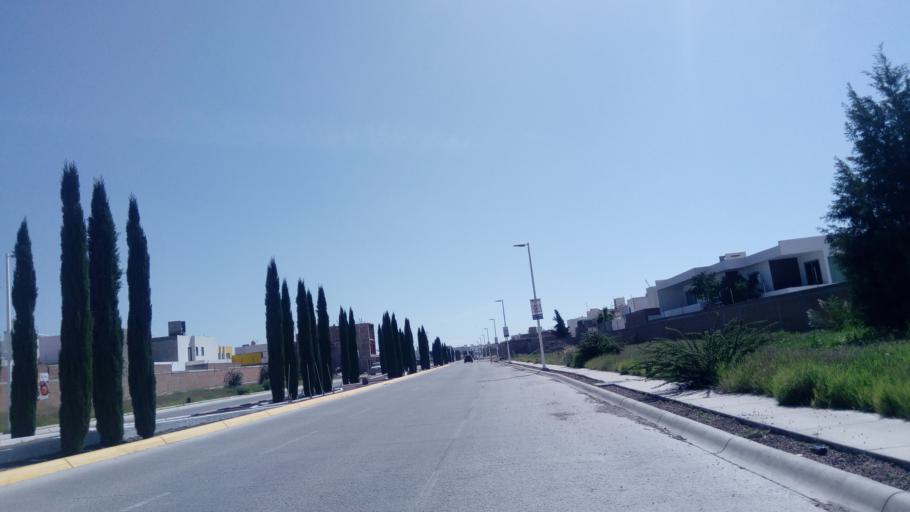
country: MX
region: Durango
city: Victoria de Durango
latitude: 23.9998
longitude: -104.6368
